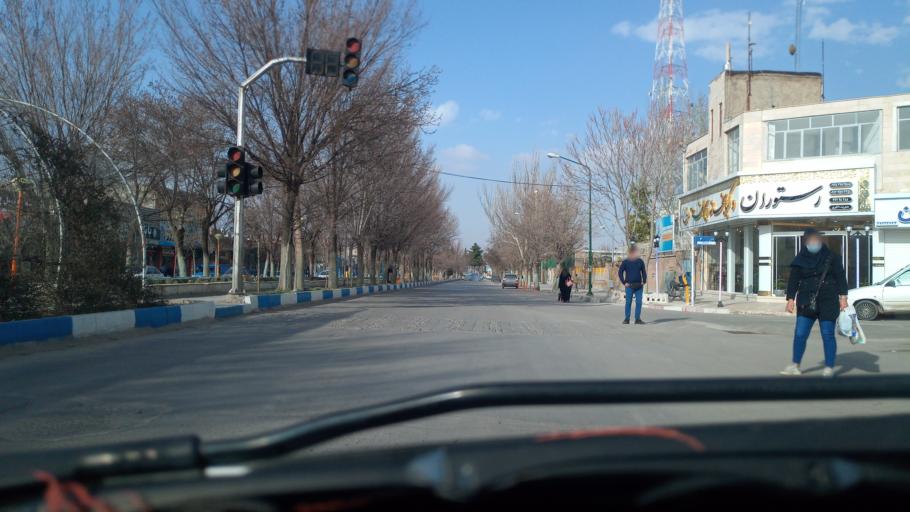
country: IR
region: Razavi Khorasan
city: Quchan
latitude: 37.0986
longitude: 58.5036
